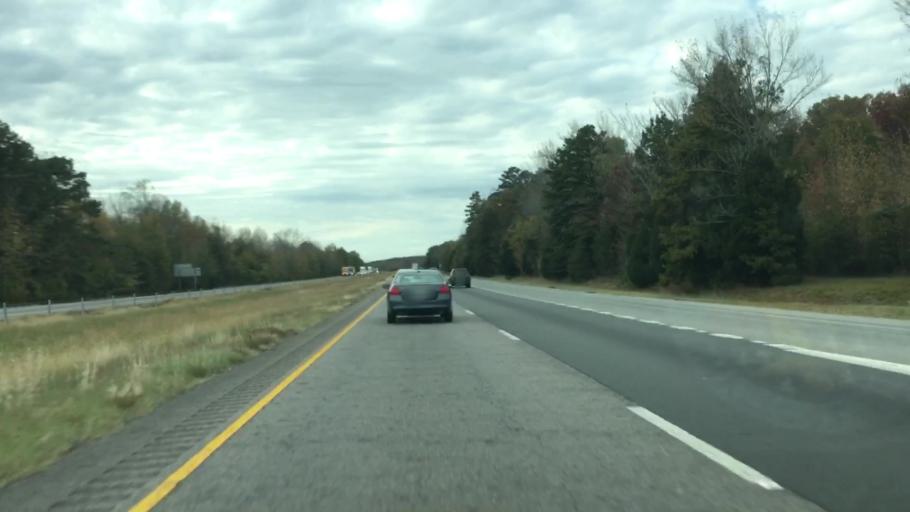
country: US
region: Arkansas
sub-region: Faulkner County
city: Conway
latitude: 35.1543
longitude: -92.5570
